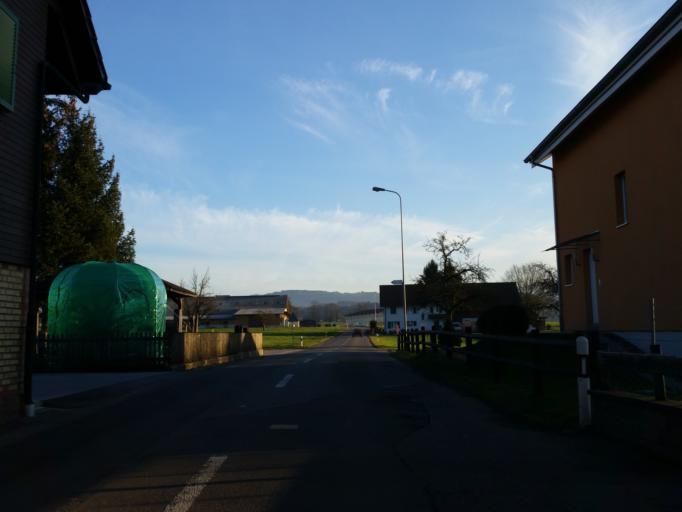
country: CH
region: Thurgau
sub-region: Weinfelden District
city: Erlen
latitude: 47.5131
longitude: 9.2627
